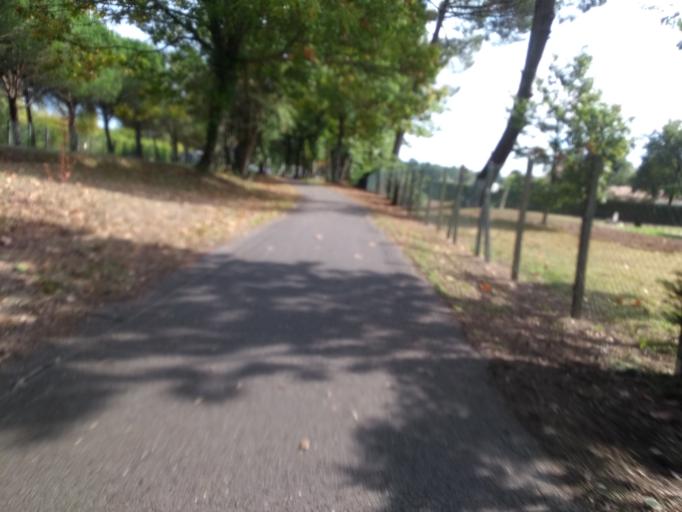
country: FR
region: Aquitaine
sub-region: Departement de la Gironde
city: Cestas
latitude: 44.7426
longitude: -0.6526
